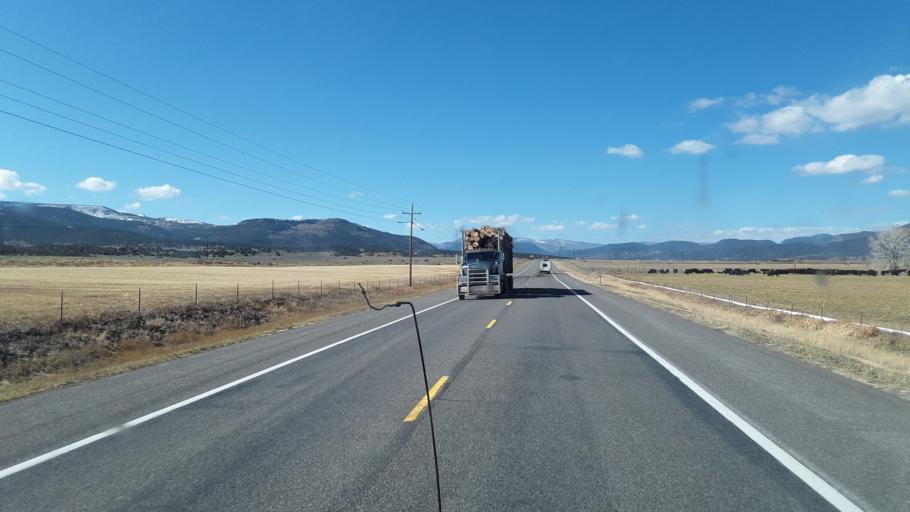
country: US
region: Colorado
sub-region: Rio Grande County
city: Del Norte
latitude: 37.6771
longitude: -106.4851
